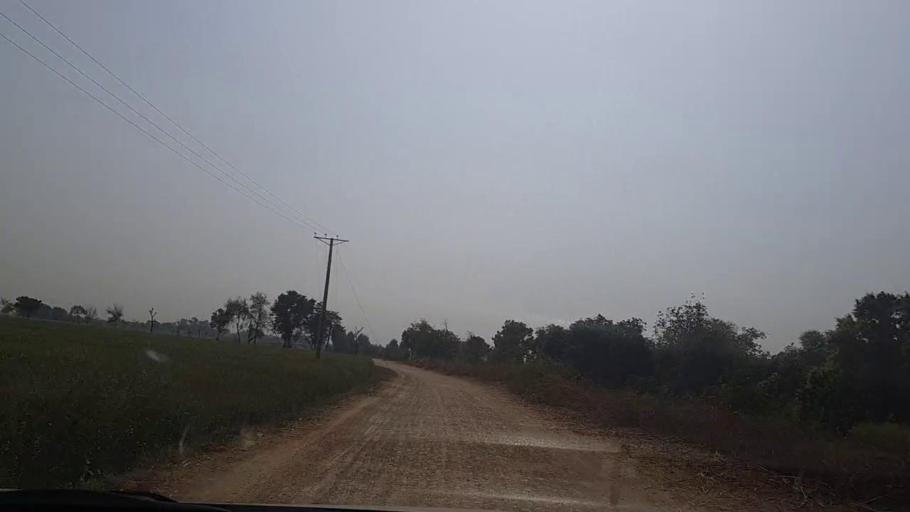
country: PK
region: Sindh
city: Pithoro
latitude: 25.5537
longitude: 69.2484
